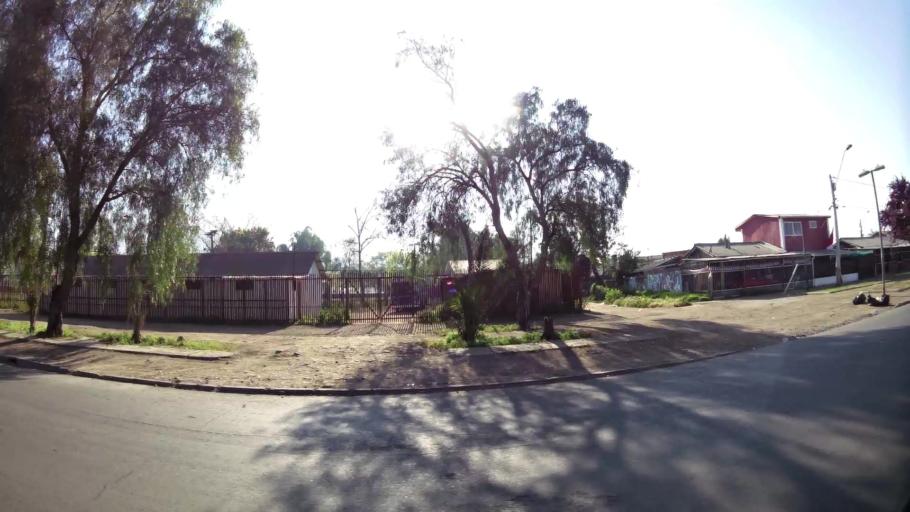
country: CL
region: Santiago Metropolitan
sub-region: Provincia de Santiago
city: Santiago
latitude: -33.3758
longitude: -70.6618
